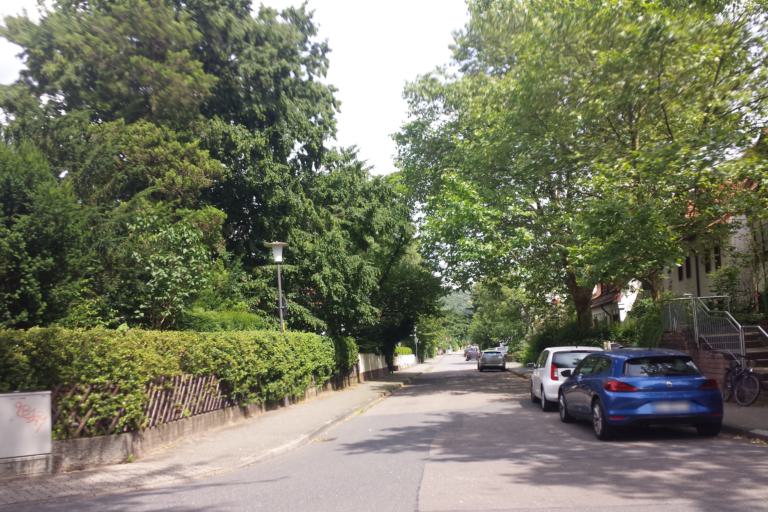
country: DE
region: Baden-Wuerttemberg
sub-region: Karlsruhe Region
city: Heidelberg
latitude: 49.4157
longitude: 8.6792
